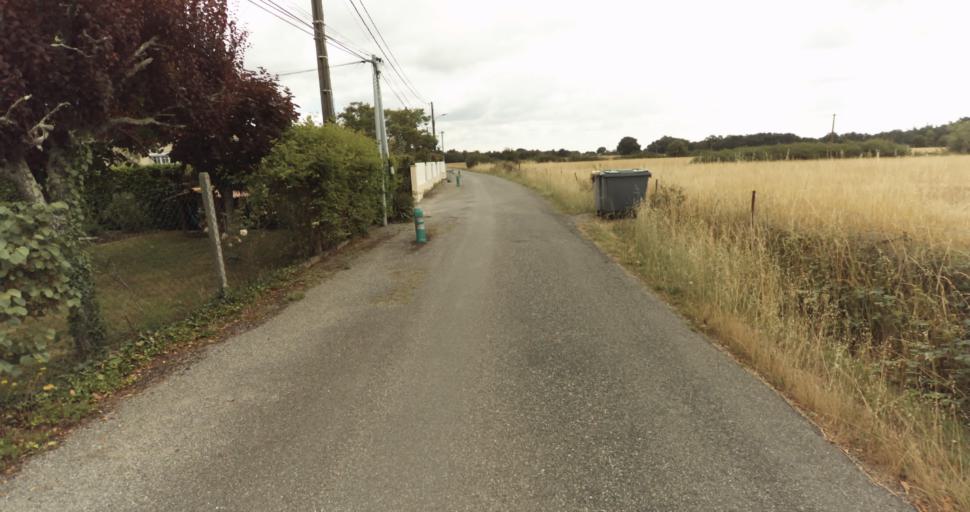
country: FR
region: Midi-Pyrenees
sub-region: Departement de la Haute-Garonne
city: Fonsorbes
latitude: 43.5467
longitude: 1.2149
